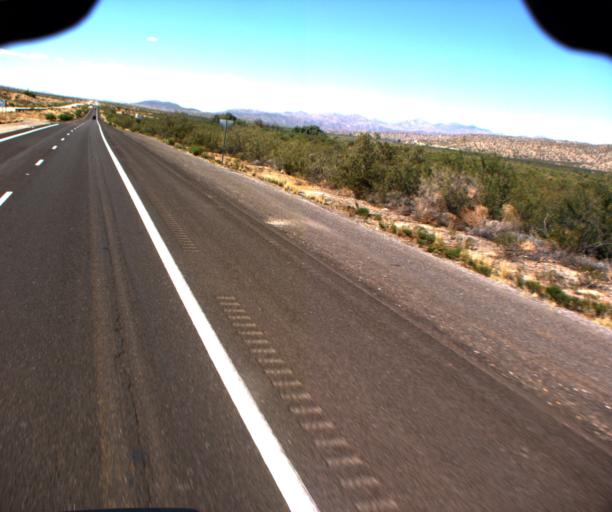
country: US
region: Arizona
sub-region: Yavapai County
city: Bagdad
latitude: 34.8382
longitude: -113.6334
